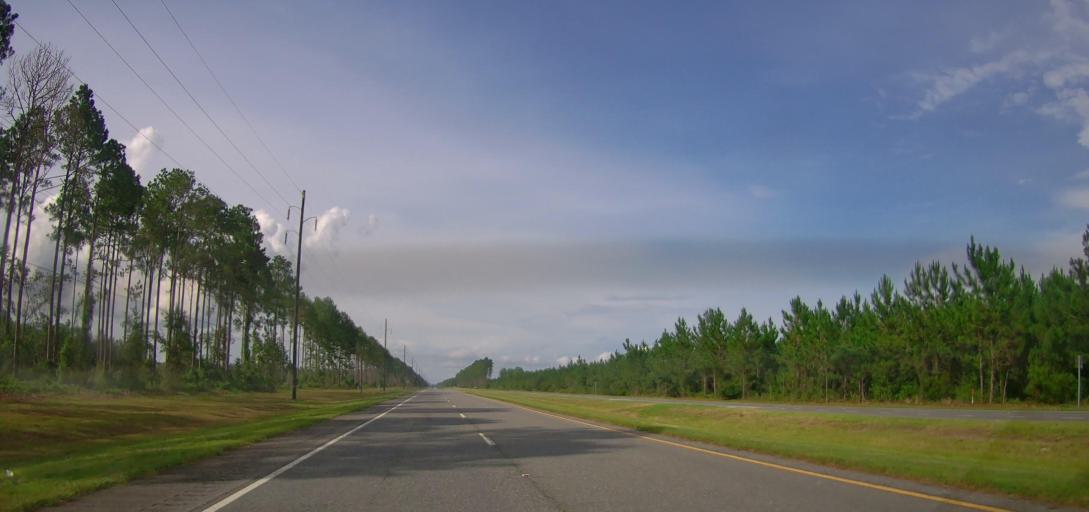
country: US
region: Georgia
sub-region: Wayne County
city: Jesup
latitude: 31.5360
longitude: -81.9814
